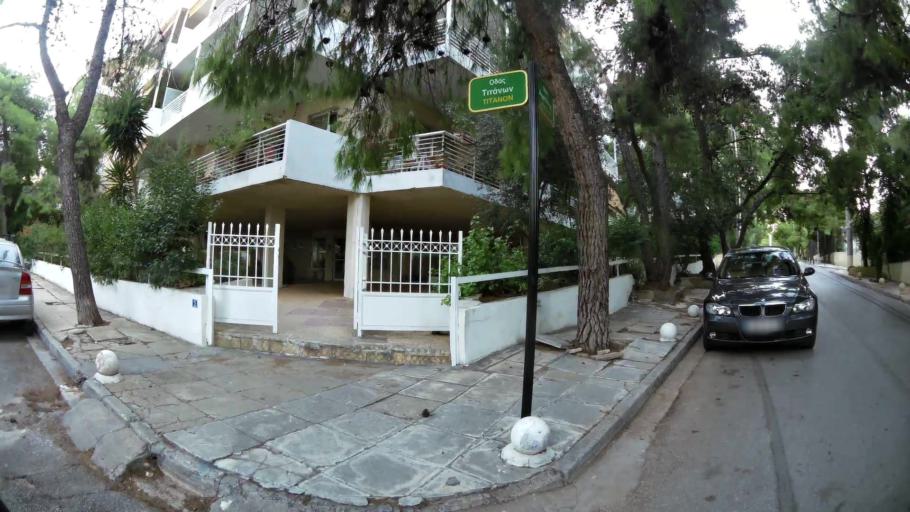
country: GR
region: Attica
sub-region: Nomarchia Anatolikis Attikis
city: Vari
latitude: 37.8205
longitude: 23.7958
